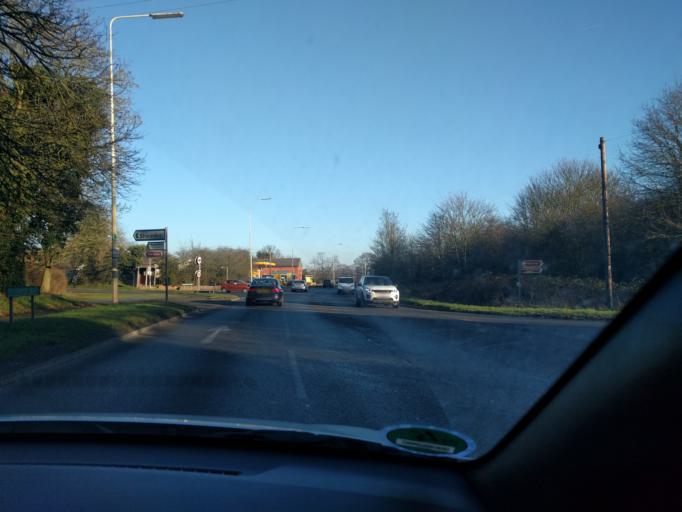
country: GB
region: England
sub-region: Staffordshire
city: Featherstone
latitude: 52.6522
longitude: -2.0797
